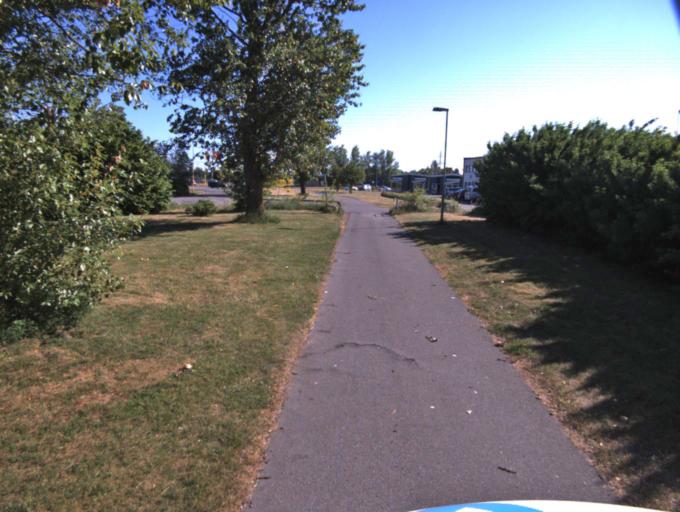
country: SE
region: Skane
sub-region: Kristianstads Kommun
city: Ahus
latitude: 55.9326
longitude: 14.2849
